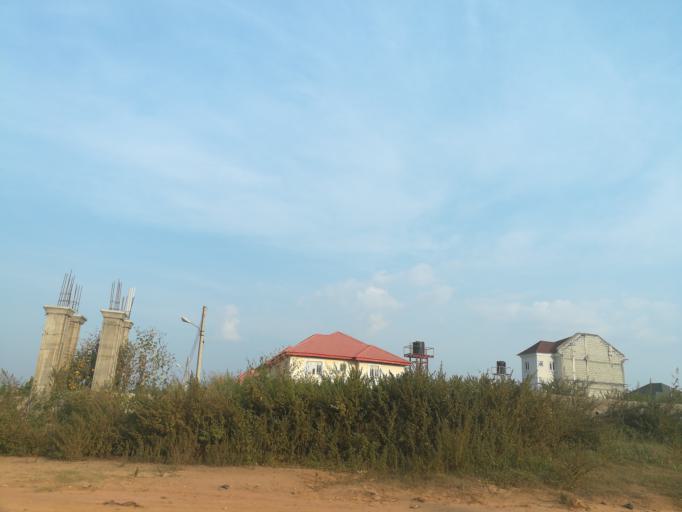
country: NG
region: Abuja Federal Capital Territory
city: Abuja
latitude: 9.1002
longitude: 7.3699
